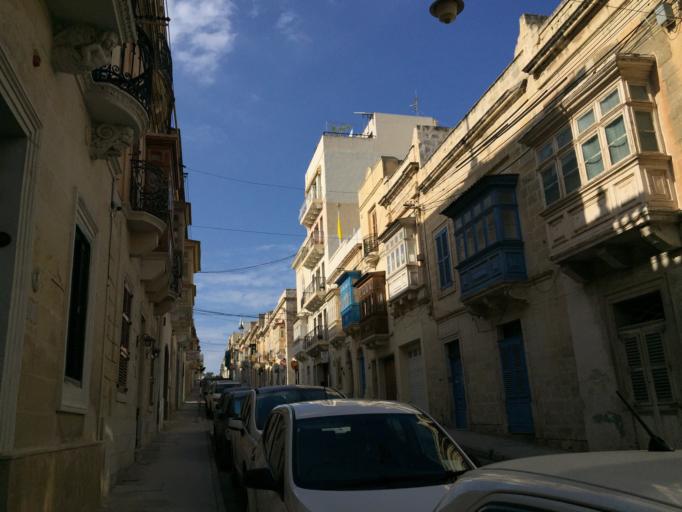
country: MT
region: Tas-Sliema
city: Sliema
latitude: 35.9098
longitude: 14.5014
